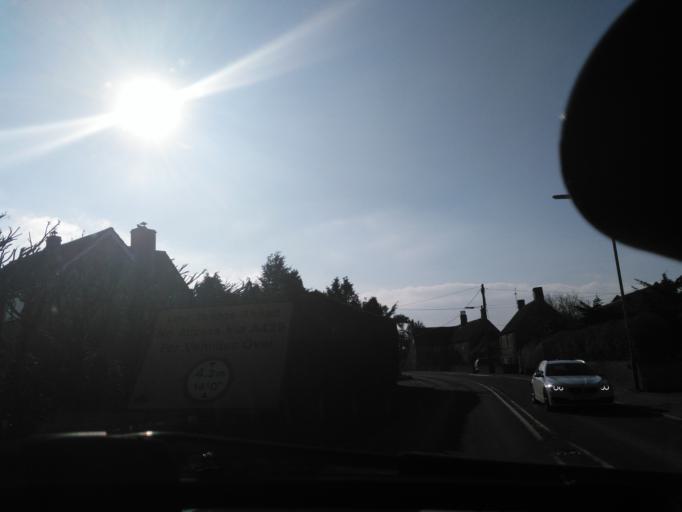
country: GB
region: England
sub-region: Wiltshire
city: Malmesbury
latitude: 51.5540
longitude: -2.1099
